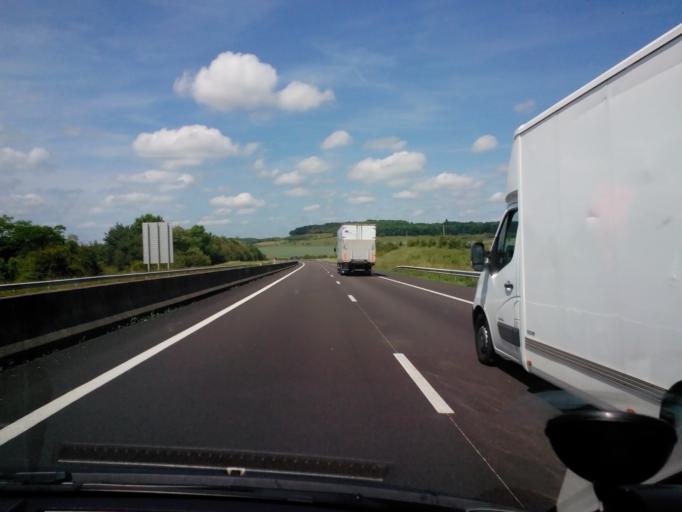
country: FR
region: Champagne-Ardenne
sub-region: Departement de la Haute-Marne
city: Nogent-le-Bas
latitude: 47.9550
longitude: 5.4179
